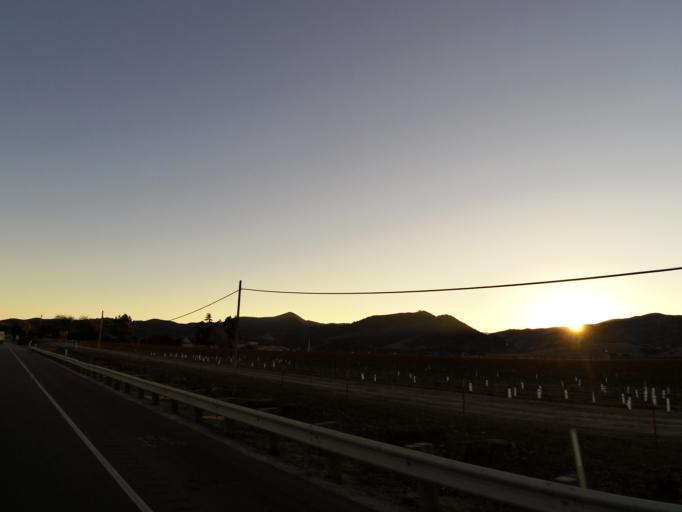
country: US
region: California
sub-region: Monterey County
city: King City
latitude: 36.2360
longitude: -121.1748
